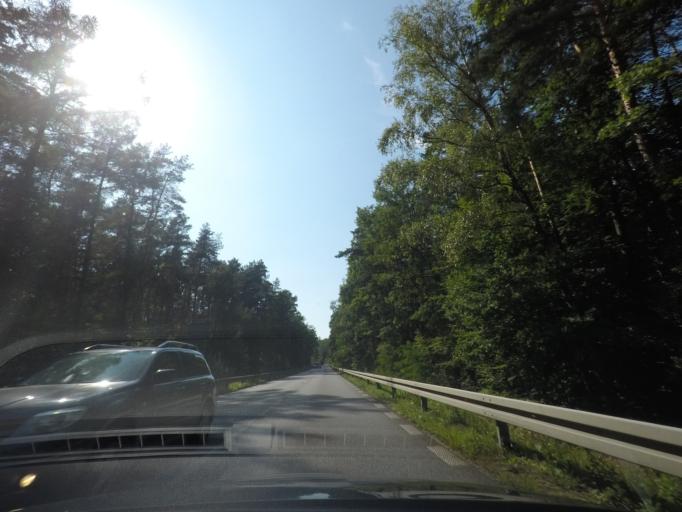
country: PL
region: Silesian Voivodeship
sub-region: Powiat pszczynski
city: Kryry
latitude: 50.0263
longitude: 18.8135
